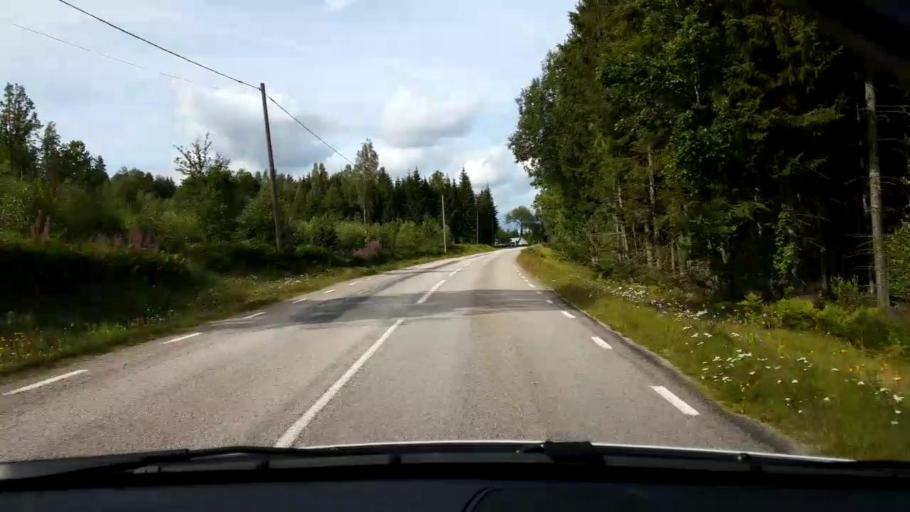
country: SE
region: Joenkoeping
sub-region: Vetlanda Kommun
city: Vetlanda
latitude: 57.3385
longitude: 15.0755
